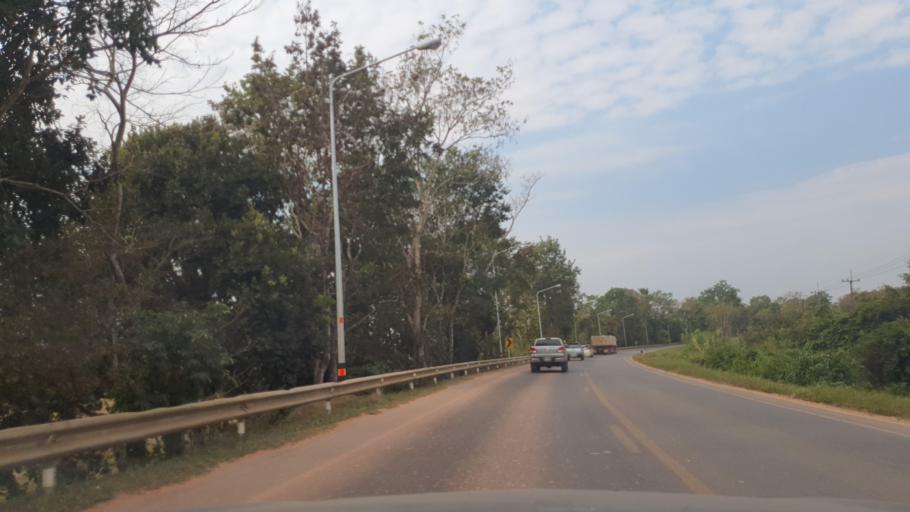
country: TH
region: Changwat Bueng Kan
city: Si Wilai
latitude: 18.2727
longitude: 103.8349
